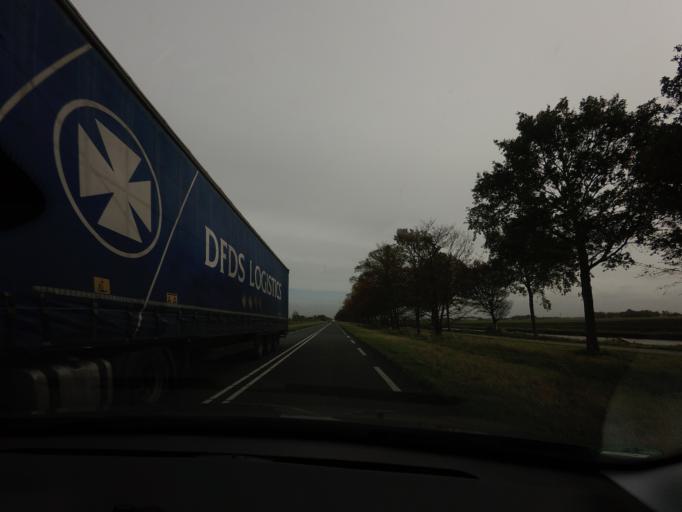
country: NL
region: Flevoland
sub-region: Gemeente Noordoostpolder
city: Emmeloord
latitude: 52.7087
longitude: 5.7967
